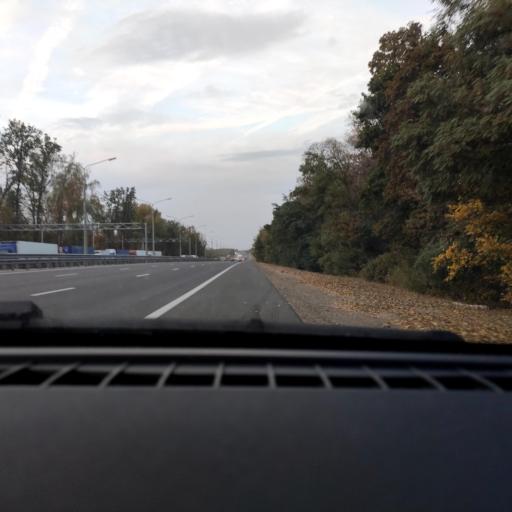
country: RU
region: Voronezj
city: Podgornoye
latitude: 51.8175
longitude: 39.2087
